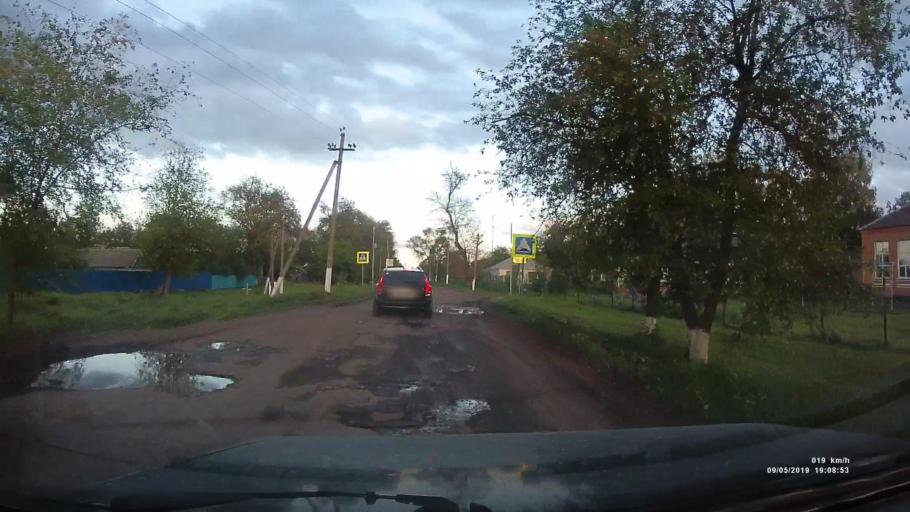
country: RU
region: Krasnodarskiy
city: Kanelovskaya
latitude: 46.7282
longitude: 39.2067
